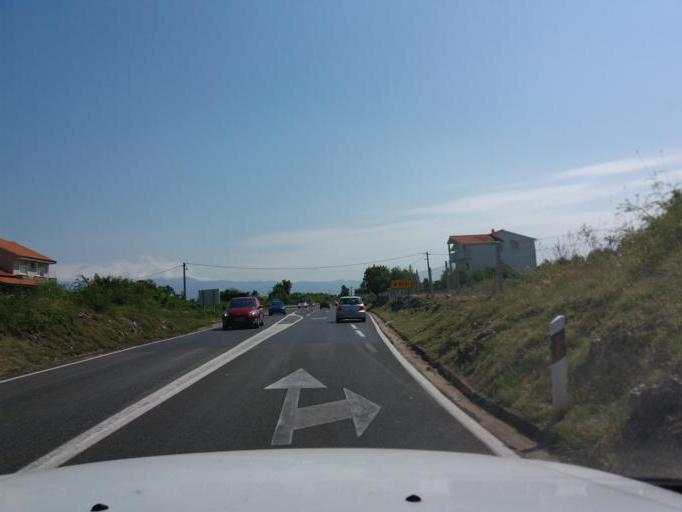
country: HR
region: Zadarska
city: Policnik
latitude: 44.1478
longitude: 15.3251
